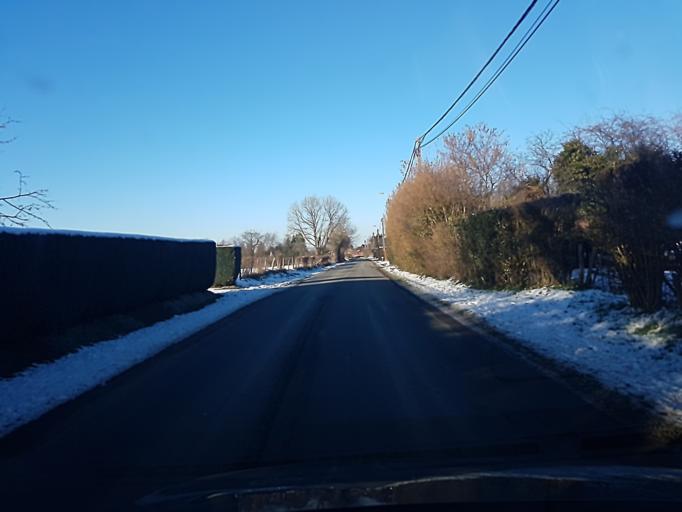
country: BE
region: Wallonia
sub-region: Province de Liege
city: Jalhay
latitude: 50.5536
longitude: 5.9664
